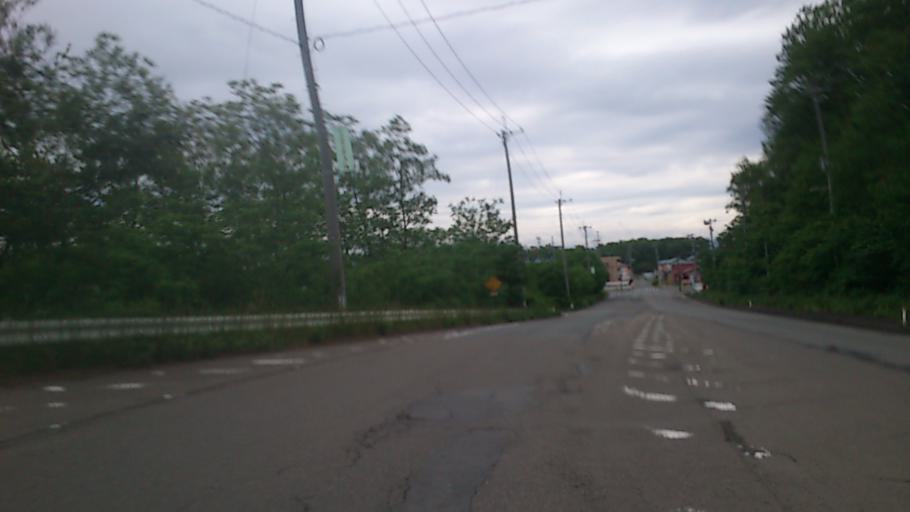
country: JP
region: Akita
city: Noshiromachi
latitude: 40.1881
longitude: 140.0101
